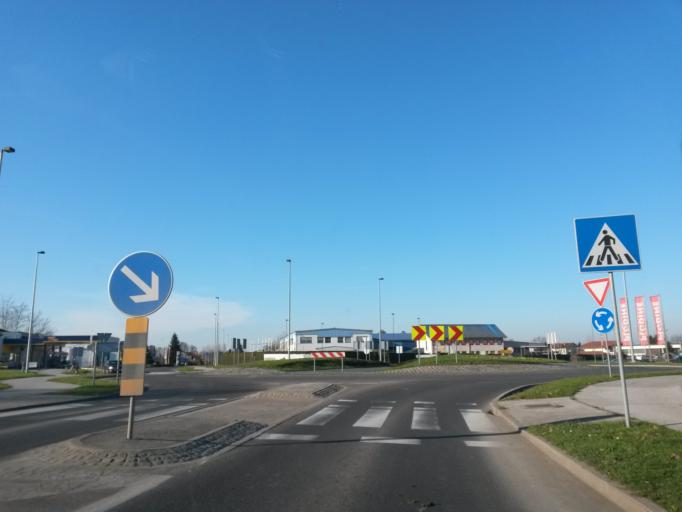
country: HR
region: Varazdinska
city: Ludbreg
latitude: 46.2418
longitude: 16.6294
